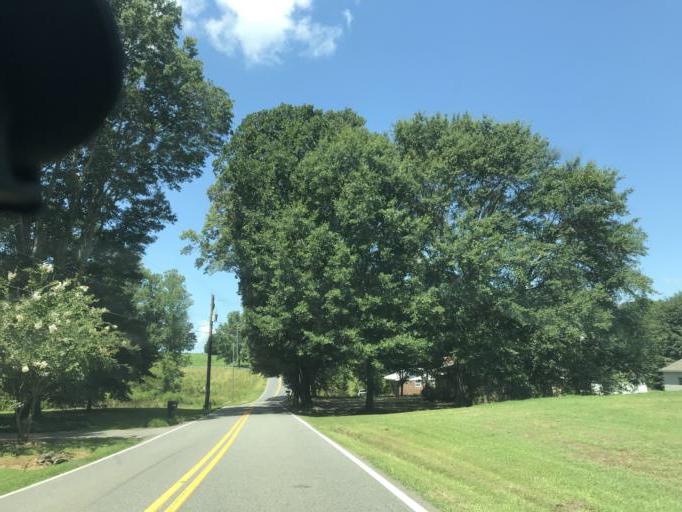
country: US
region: Georgia
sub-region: Forsyth County
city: Cumming
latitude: 34.2804
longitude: -84.0928
